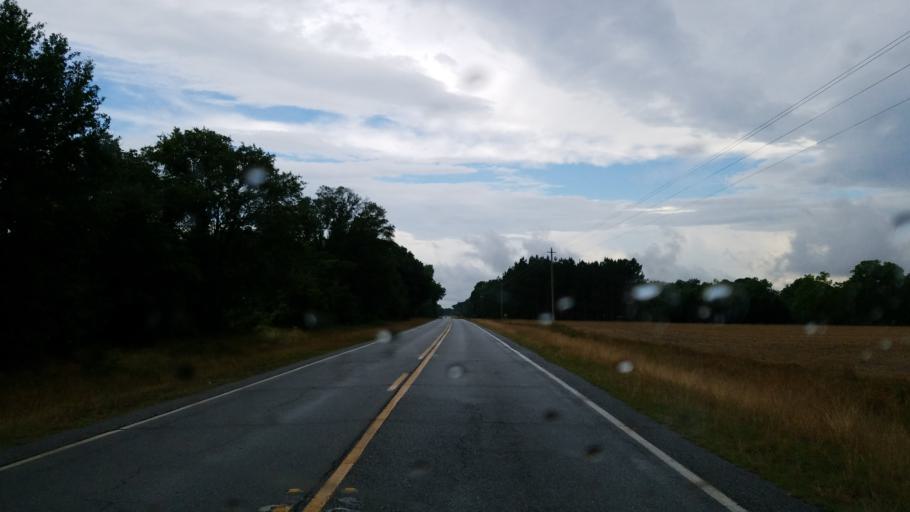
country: US
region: Georgia
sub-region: Crisp County
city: Cordele
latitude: 31.8949
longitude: -83.7673
